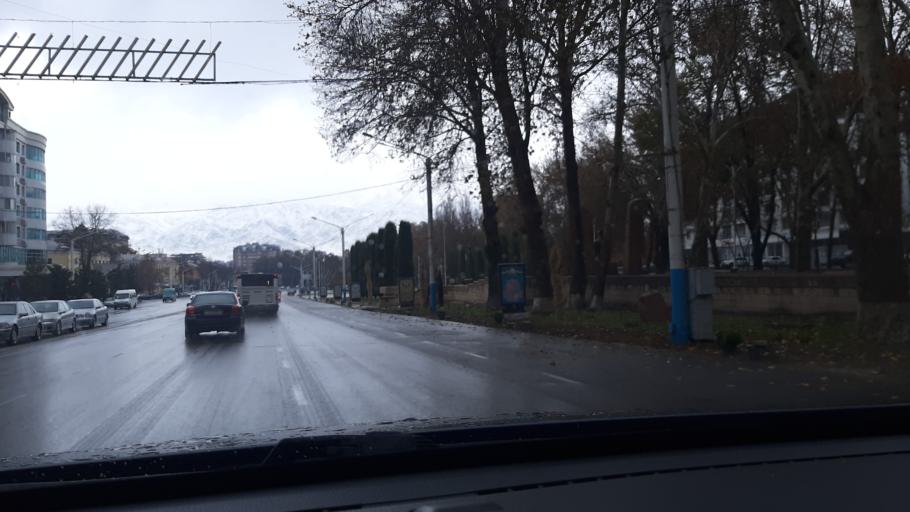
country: TJ
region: Viloyati Sughd
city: Khujand
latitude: 40.2822
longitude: 69.6246
